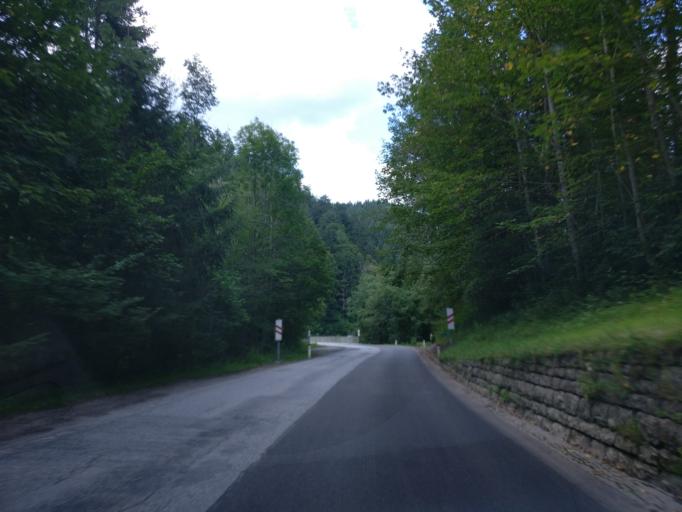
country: AT
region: Styria
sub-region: Politischer Bezirk Liezen
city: Johnsbach
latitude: 47.5898
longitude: 14.6278
